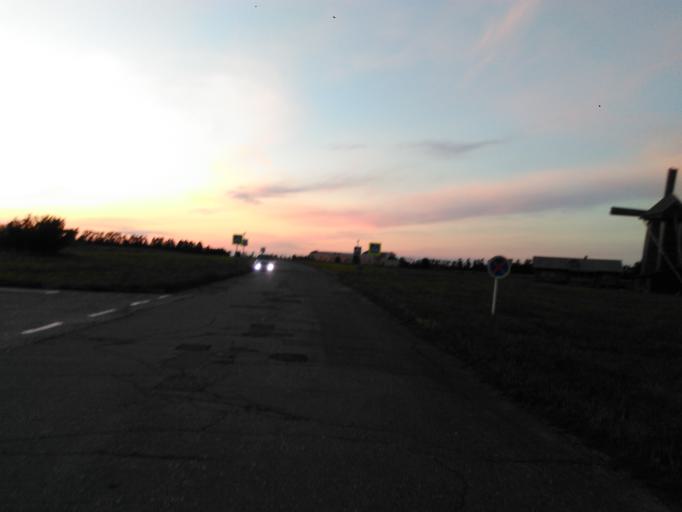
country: RU
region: Penza
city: Lermontovo
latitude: 52.9960
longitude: 43.6730
